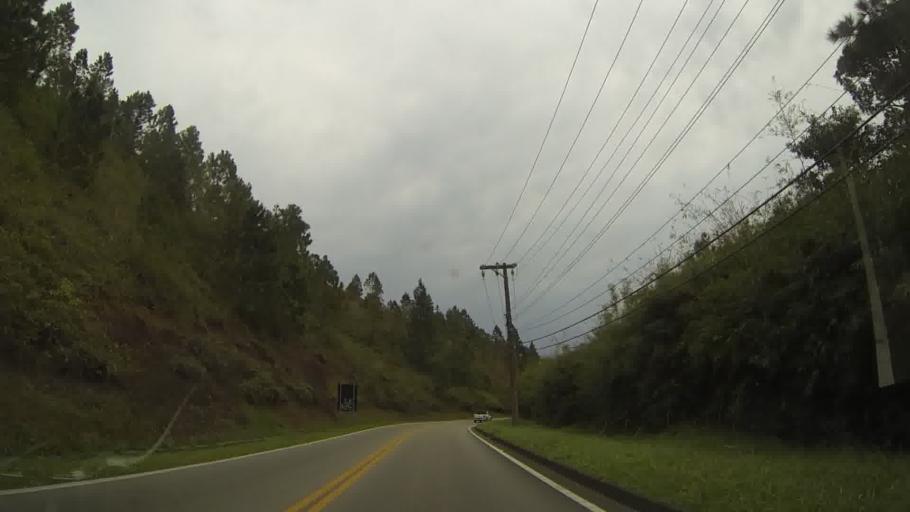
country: BR
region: Sao Paulo
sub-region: Sao Sebastiao
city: Sao Sebastiao
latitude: -23.8294
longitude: -45.5162
